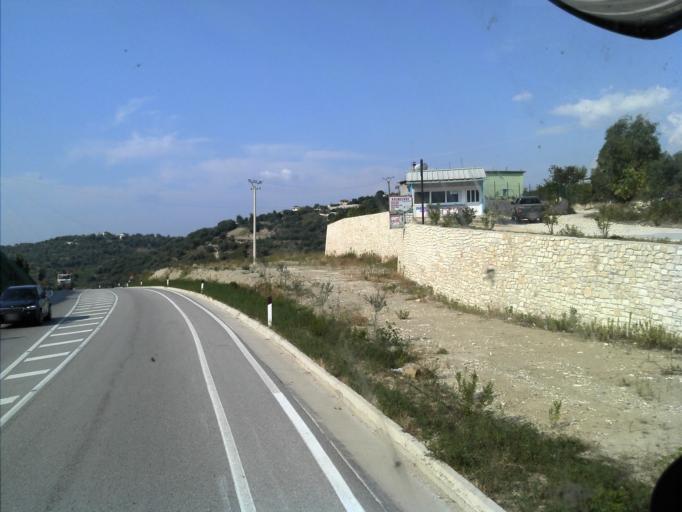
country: AL
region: Fier
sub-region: Rrethi i Mallakastres
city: Fratar
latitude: 40.4909
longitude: 19.8401
